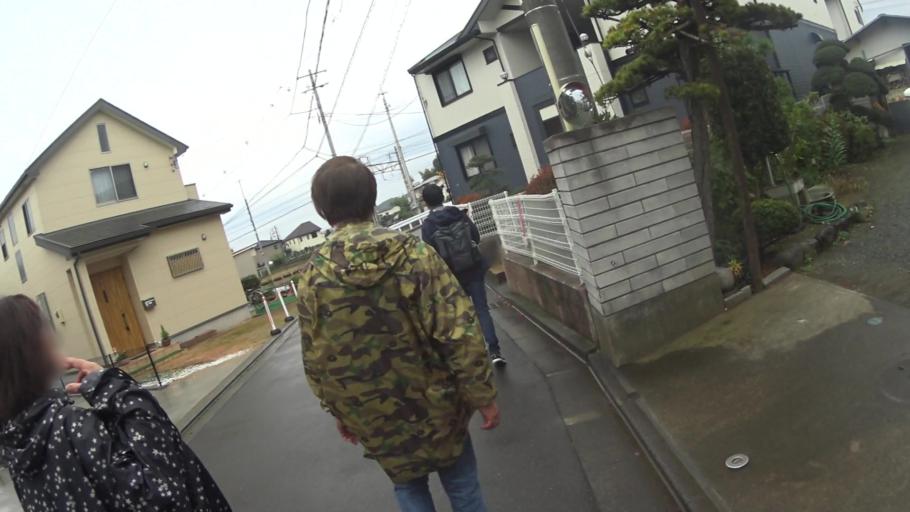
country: JP
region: Kanagawa
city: Hadano
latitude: 35.3724
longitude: 139.2133
